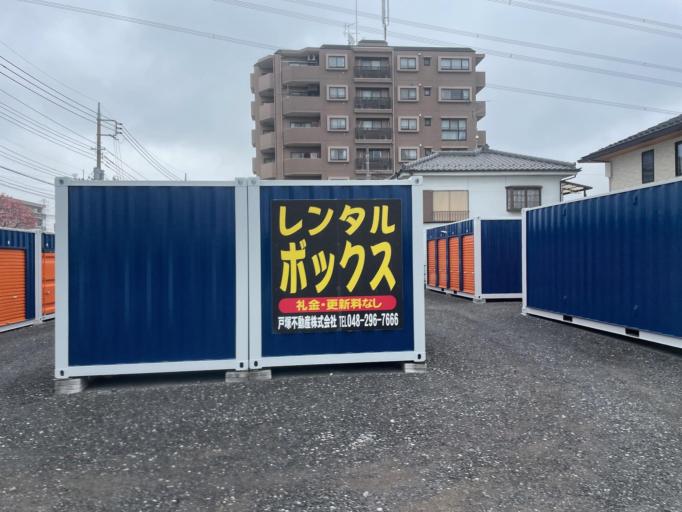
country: JP
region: Saitama
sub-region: Kawaguchi-shi
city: Hatogaya-honcho
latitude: 35.8703
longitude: 139.7421
